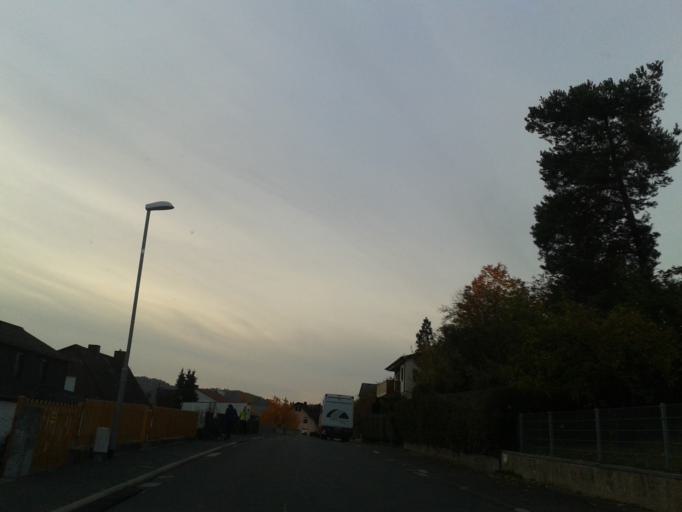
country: DE
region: Hesse
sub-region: Regierungsbezirk Giessen
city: Sinn
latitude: 50.6491
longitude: 8.3369
